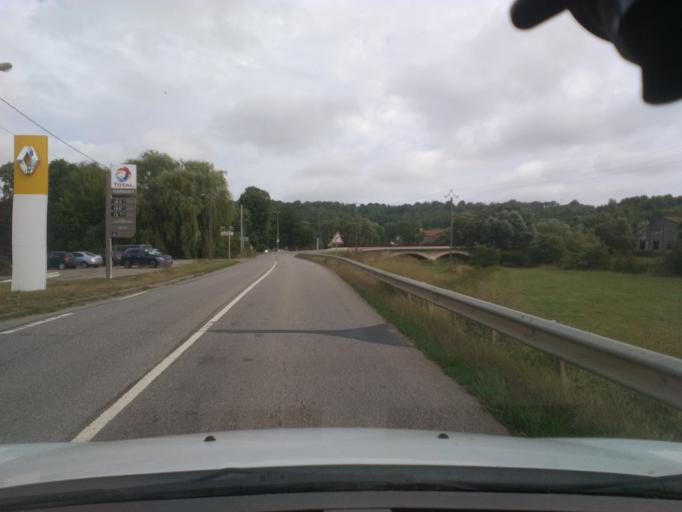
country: FR
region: Lorraine
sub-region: Departement de Meurthe-et-Moselle
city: Pulligny
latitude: 48.5227
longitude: 6.1583
